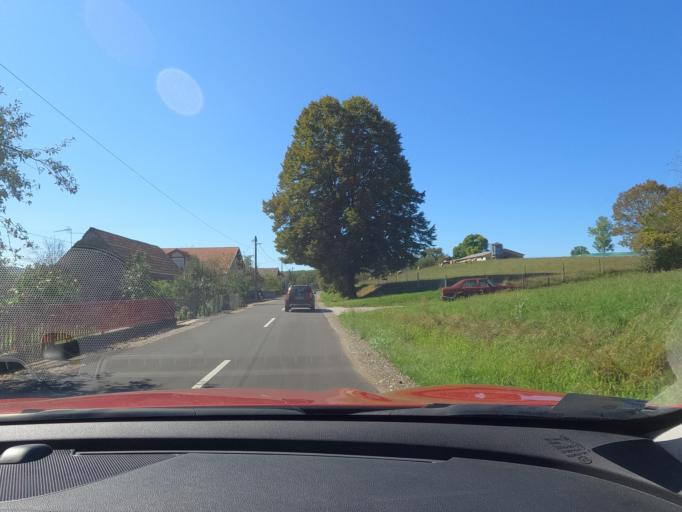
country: HR
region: Sisacko-Moslavacka
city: Petrinja
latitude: 45.4555
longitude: 16.2621
